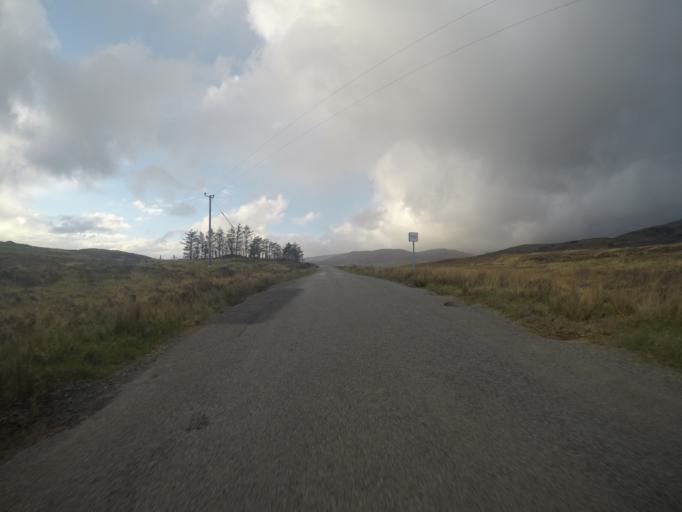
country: GB
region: Scotland
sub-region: Highland
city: Isle of Skye
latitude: 57.4578
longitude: -6.2970
